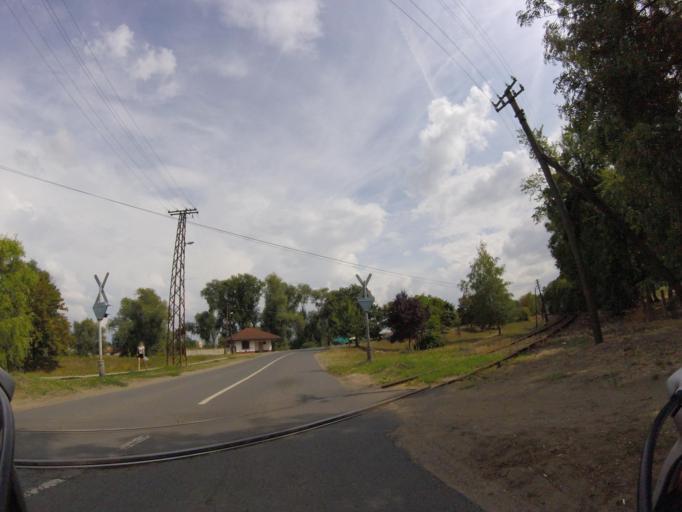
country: HU
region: Szabolcs-Szatmar-Bereg
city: Nagyecsed
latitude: 47.8633
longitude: 22.3856
